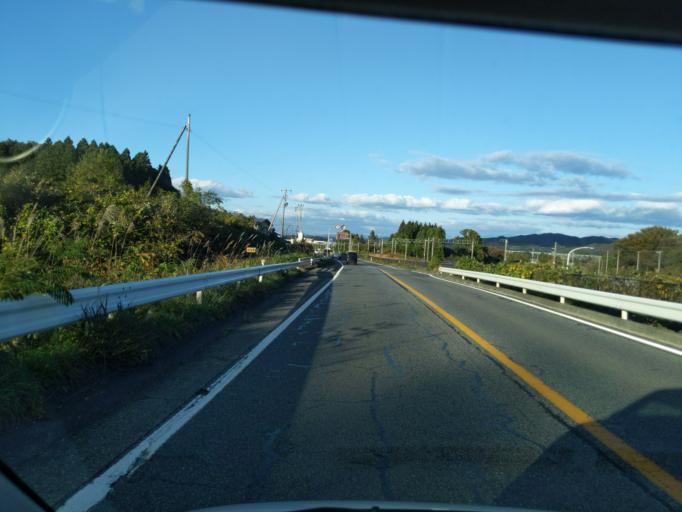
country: JP
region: Iwate
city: Kitakami
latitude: 39.2390
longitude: 141.0972
